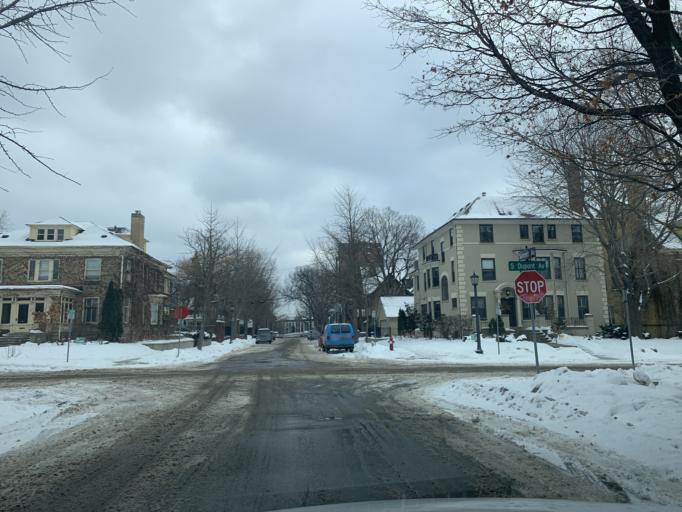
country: US
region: Minnesota
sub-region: Hennepin County
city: Minneapolis
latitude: 44.9655
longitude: -93.2934
